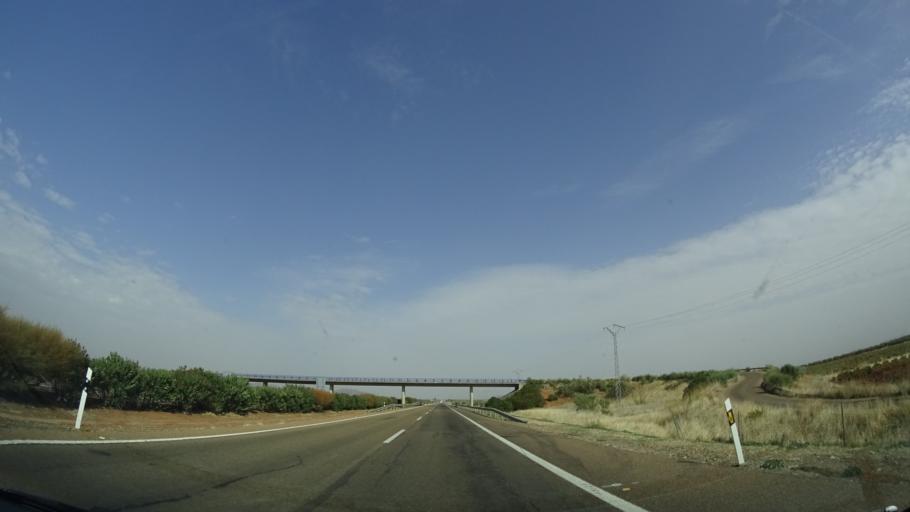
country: ES
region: Extremadura
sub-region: Provincia de Badajoz
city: Almendralejo
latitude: 38.7407
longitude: -6.3891
